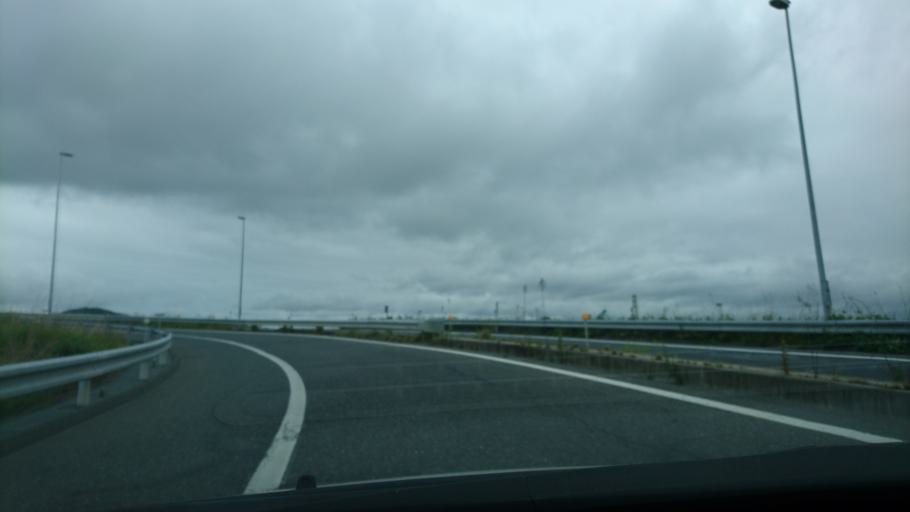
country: JP
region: Miyagi
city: Ishinomaki
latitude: 38.4984
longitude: 141.2862
